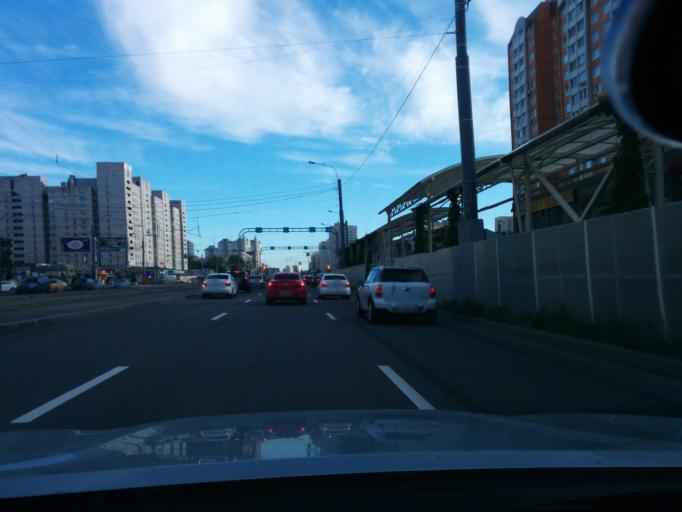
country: RU
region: Leningrad
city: Parnas
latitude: 60.0545
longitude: 30.3359
